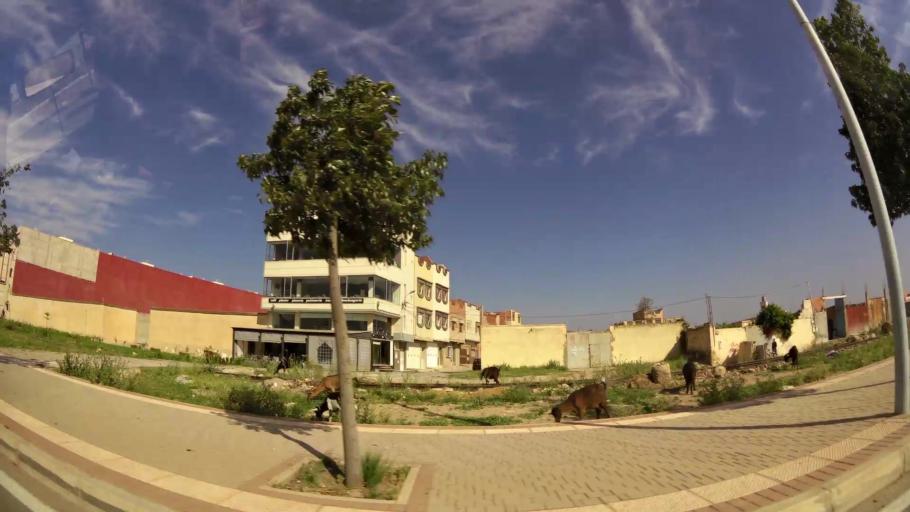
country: MA
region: Oriental
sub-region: Oujda-Angad
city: Oujda
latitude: 34.7150
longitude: -1.8843
